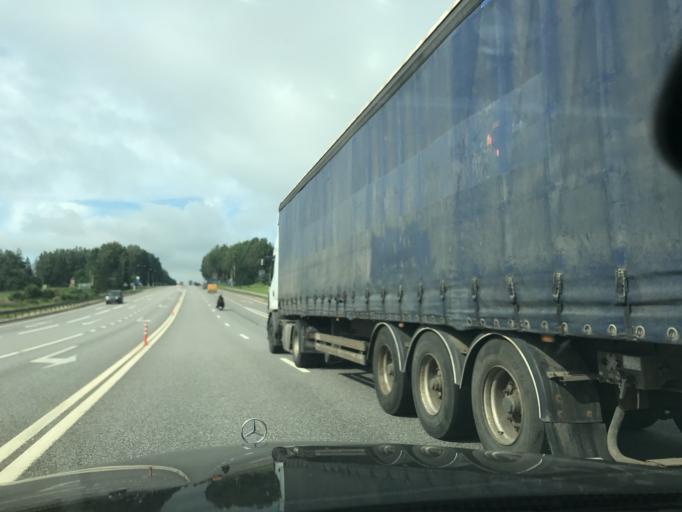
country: RU
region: Smolensk
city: Kardymovo
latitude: 55.0141
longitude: 32.2957
